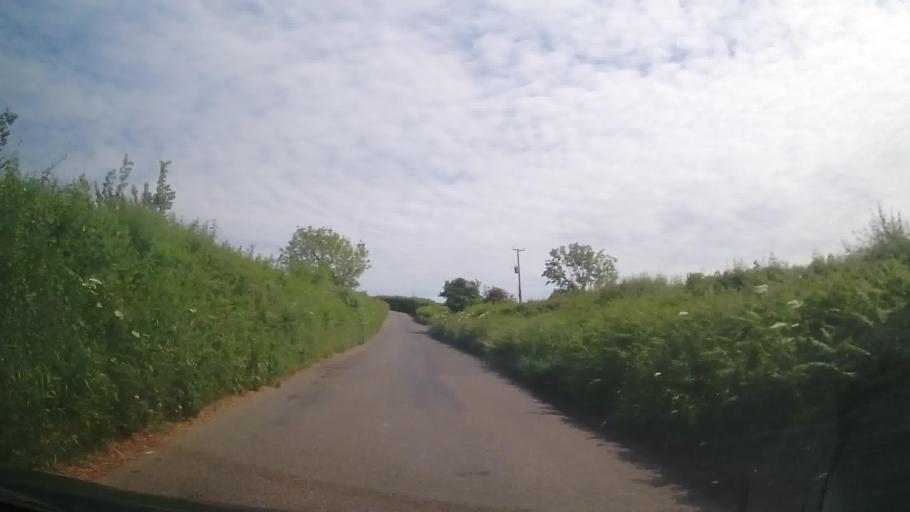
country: GB
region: England
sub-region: Devon
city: Salcombe
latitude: 50.2685
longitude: -3.6787
